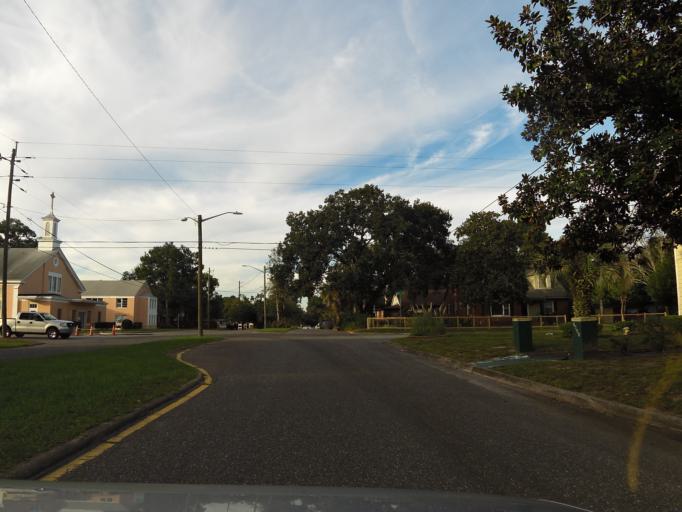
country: US
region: Florida
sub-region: Duval County
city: Jacksonville
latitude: 30.3875
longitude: -81.6567
